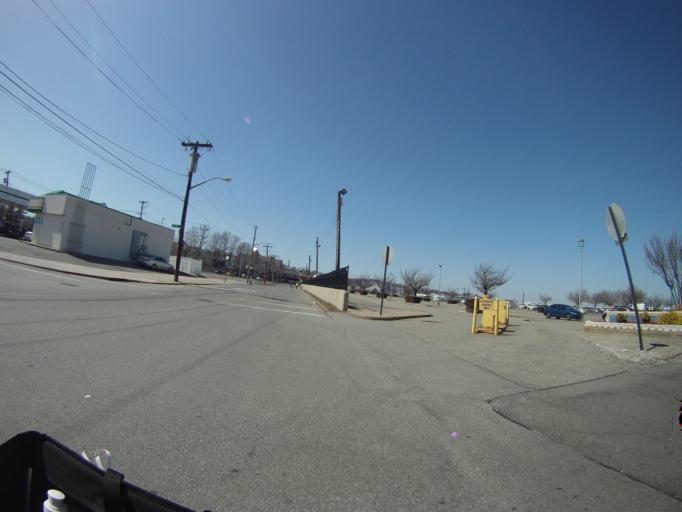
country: US
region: New Jersey
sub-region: Hudson County
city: Bayonne
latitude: 40.6195
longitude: -74.0691
